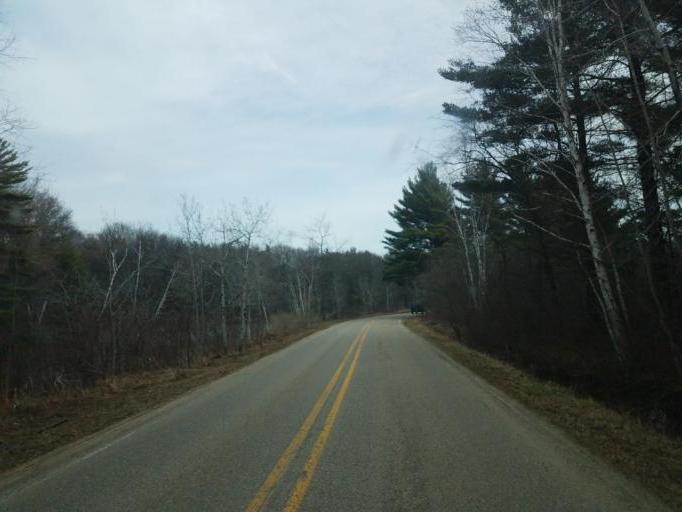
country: US
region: Michigan
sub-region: Oceana County
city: Hart
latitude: 43.6565
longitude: -86.5256
